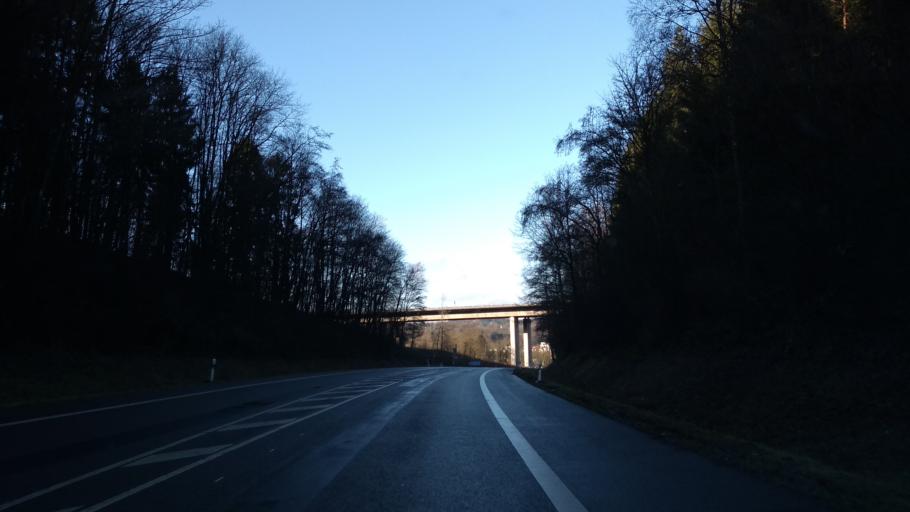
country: DE
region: North Rhine-Westphalia
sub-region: Regierungsbezirk Koln
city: Engelskirchen
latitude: 50.9795
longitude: 7.4324
